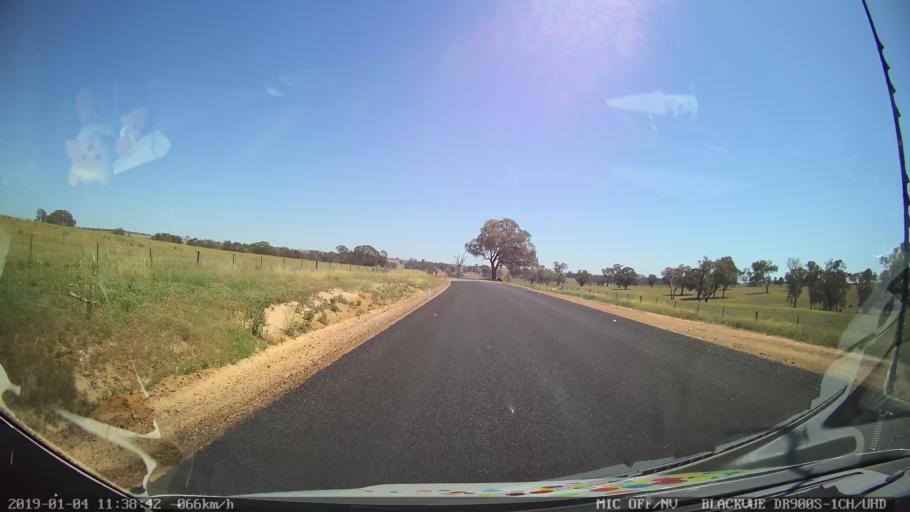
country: AU
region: New South Wales
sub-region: Cabonne
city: Molong
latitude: -33.0203
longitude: 148.8012
